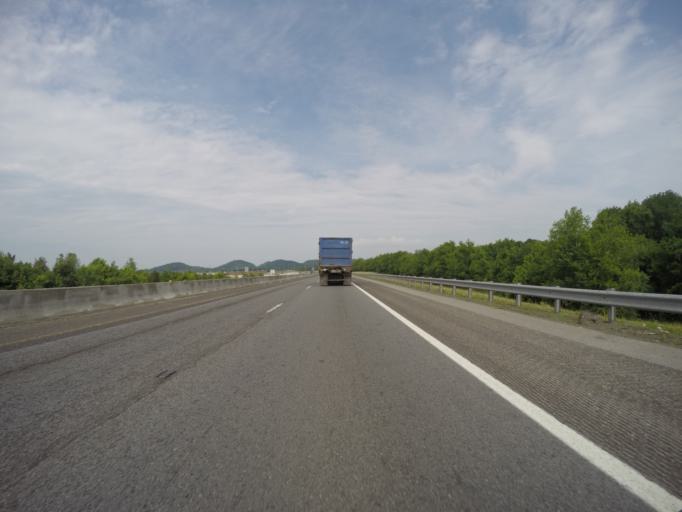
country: US
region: Tennessee
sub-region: Davidson County
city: Nashville
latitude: 36.2345
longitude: -86.8041
